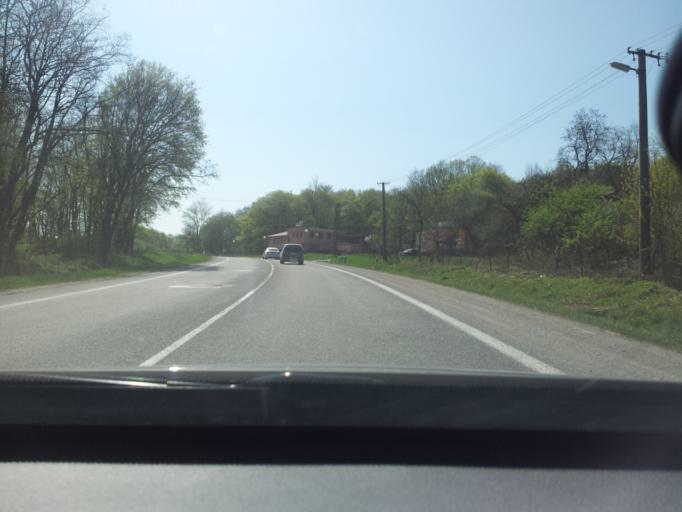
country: SK
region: Trenciansky
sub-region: Okres Trencin
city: Trencin
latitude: 48.8130
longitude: 18.0866
